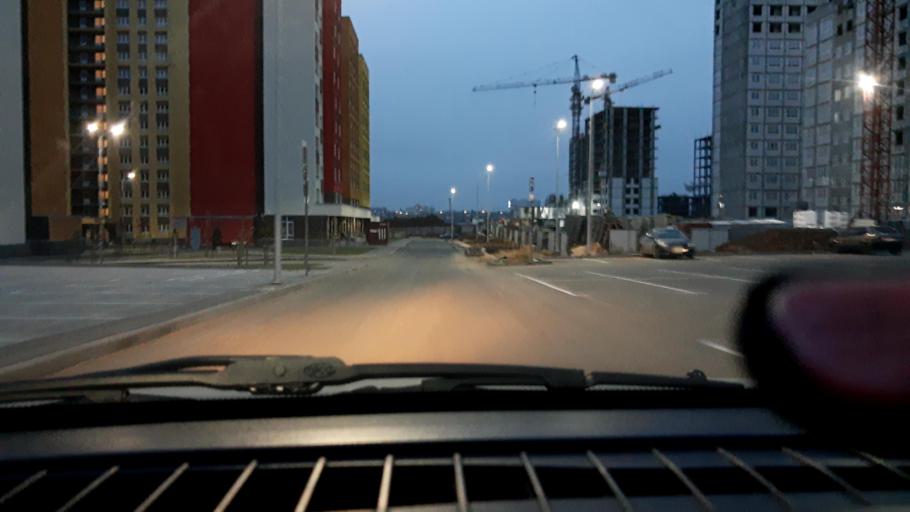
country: RU
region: Nizjnij Novgorod
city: Afonino
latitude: 56.2717
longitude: 44.0445
